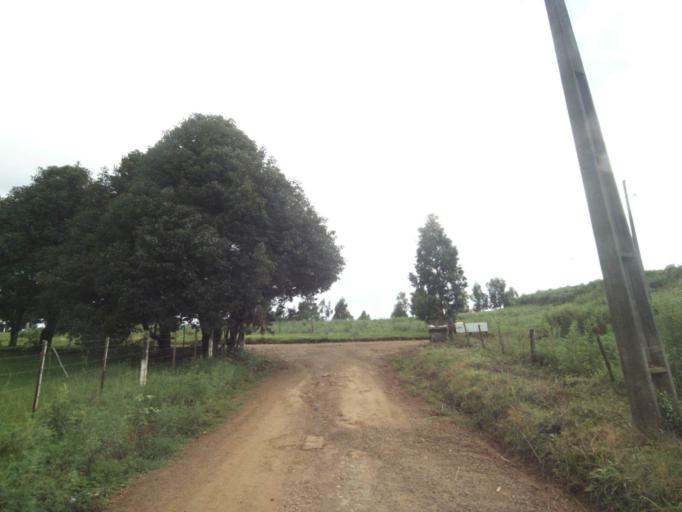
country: BR
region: Rio Grande do Sul
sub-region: Lagoa Vermelha
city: Lagoa Vermelha
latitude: -28.2034
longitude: -51.5096
